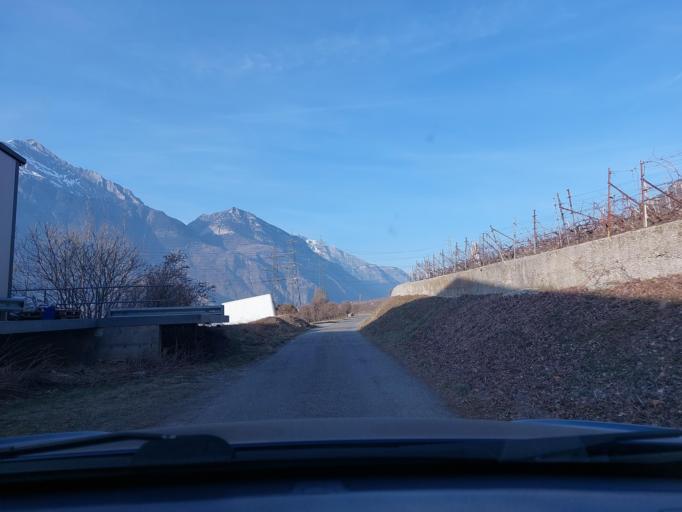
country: CH
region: Valais
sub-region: Martigny District
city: Charrat-les-Chenes
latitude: 46.1107
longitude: 7.1175
